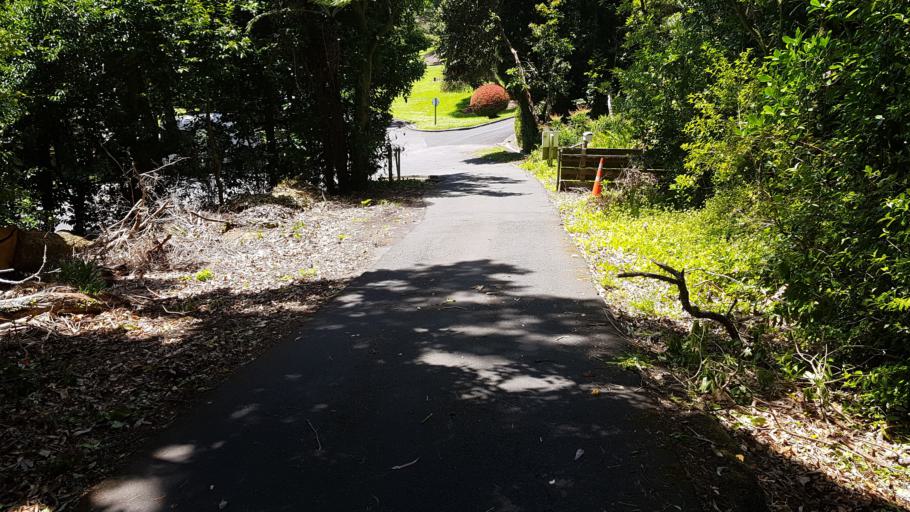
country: NZ
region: Auckland
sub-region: Auckland
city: North Shore
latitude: -36.8208
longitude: 174.7206
